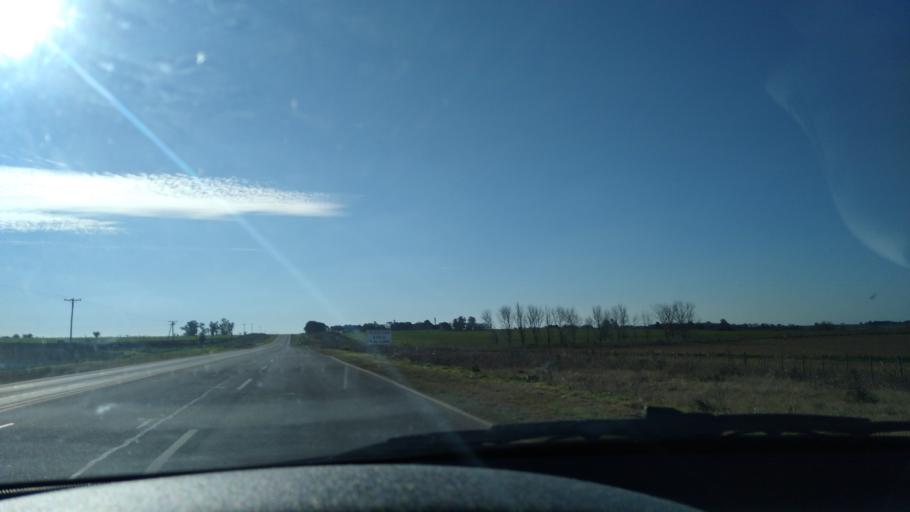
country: AR
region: Entre Rios
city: Aranguren
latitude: -32.3979
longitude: -60.3277
